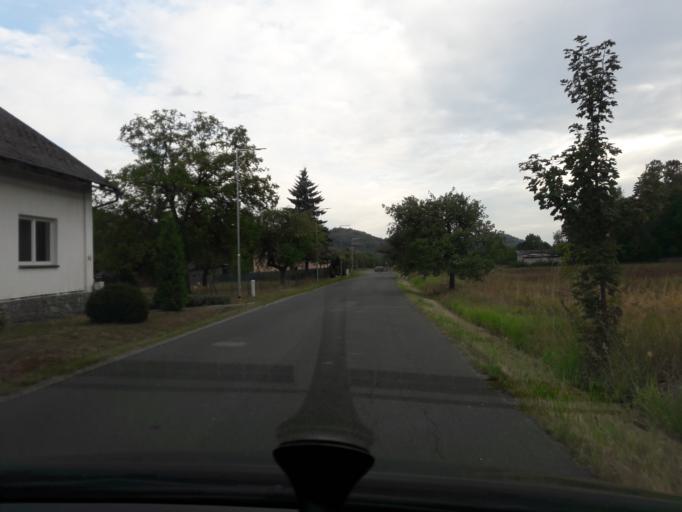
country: CZ
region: Olomoucky
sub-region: Okres Sumperk
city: Loucna nad Desnou
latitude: 50.0638
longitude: 17.0867
